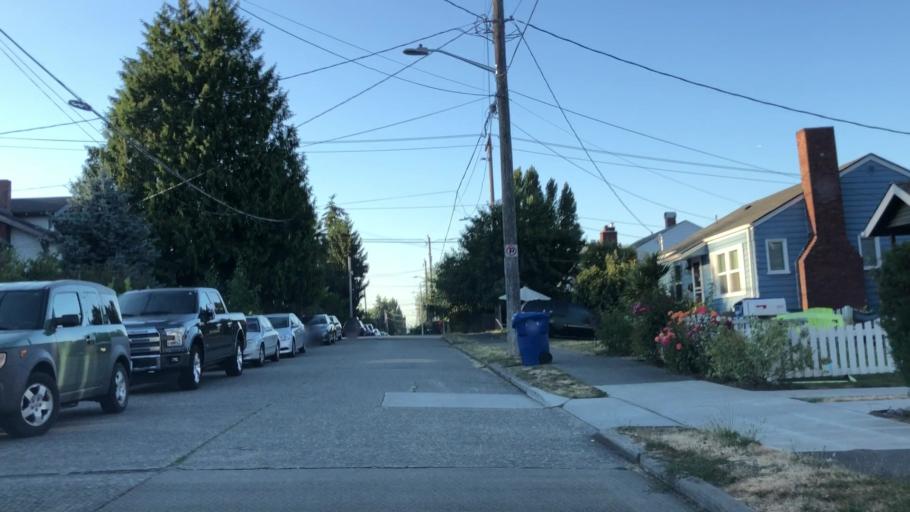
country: US
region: Washington
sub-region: King County
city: Seattle
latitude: 47.6459
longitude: -122.3833
